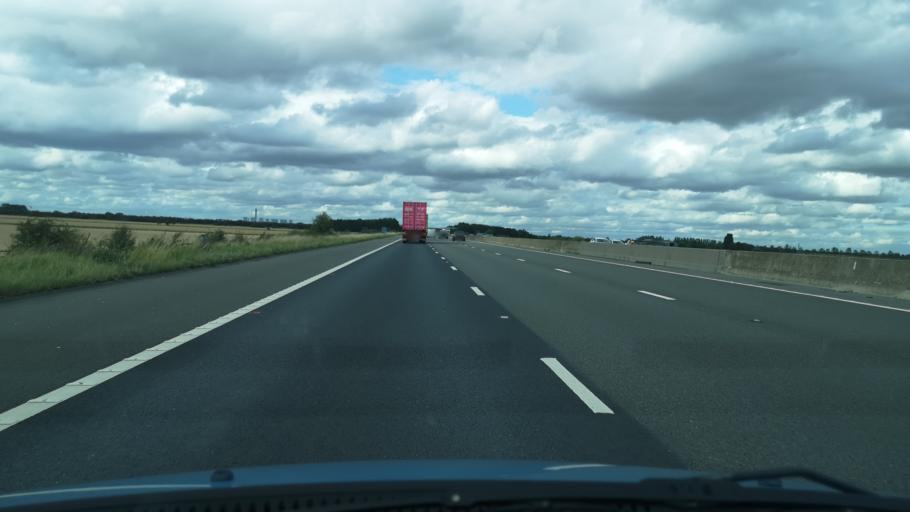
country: GB
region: England
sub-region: East Riding of Yorkshire
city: Rawcliffe
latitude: 53.6372
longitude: -0.9661
